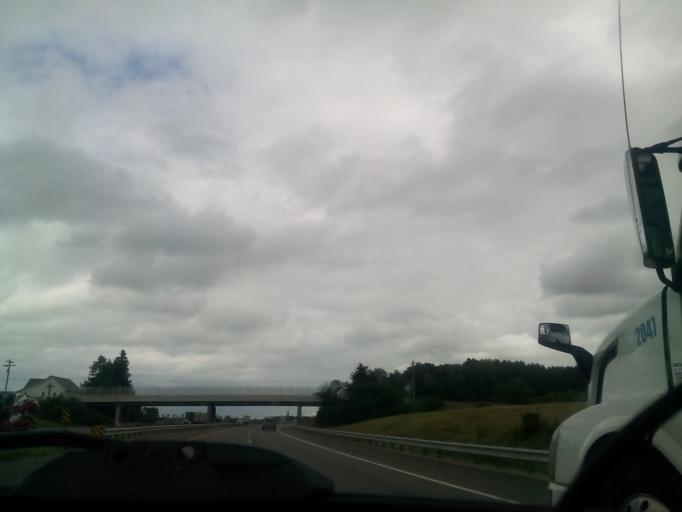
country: US
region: Indiana
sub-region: Steuben County
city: Hamilton
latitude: 41.6305
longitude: -84.7909
